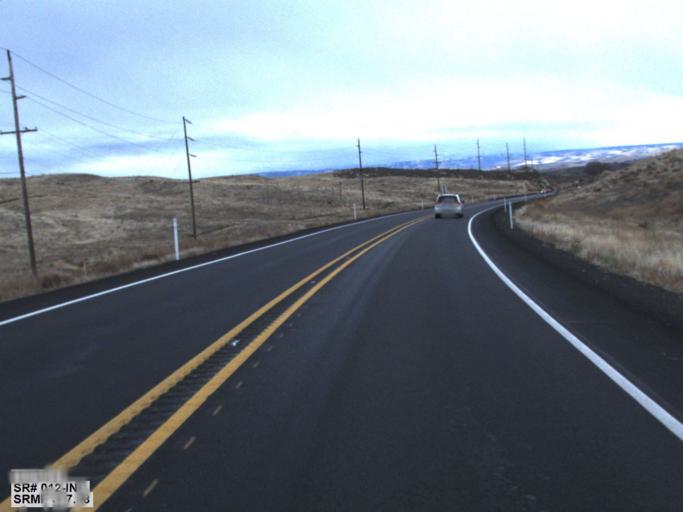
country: US
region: Washington
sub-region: Walla Walla County
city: Garrett
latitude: 46.0527
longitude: -118.7098
